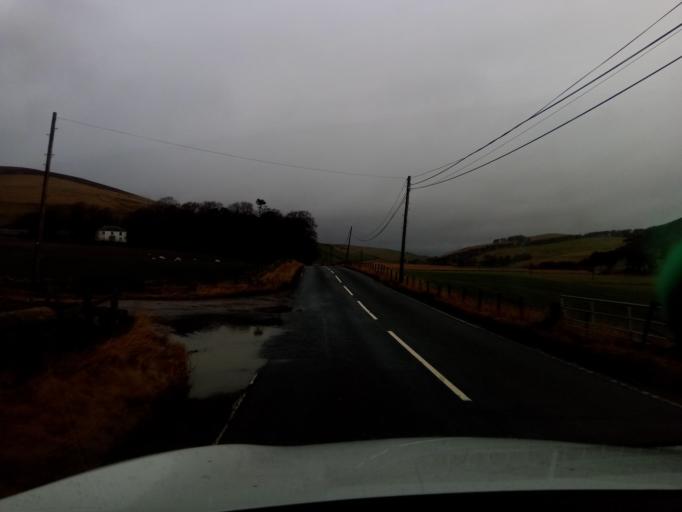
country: GB
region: Scotland
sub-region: The Scottish Borders
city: West Linton
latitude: 55.6612
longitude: -3.3150
